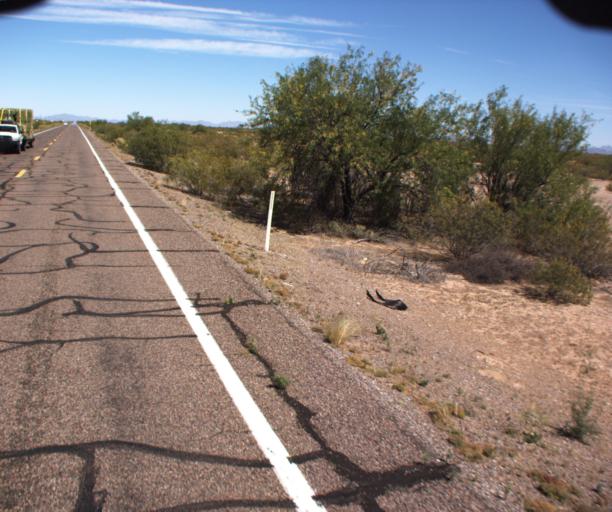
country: US
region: Arizona
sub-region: Maricopa County
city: Gila Bend
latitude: 32.8090
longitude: -112.7945
